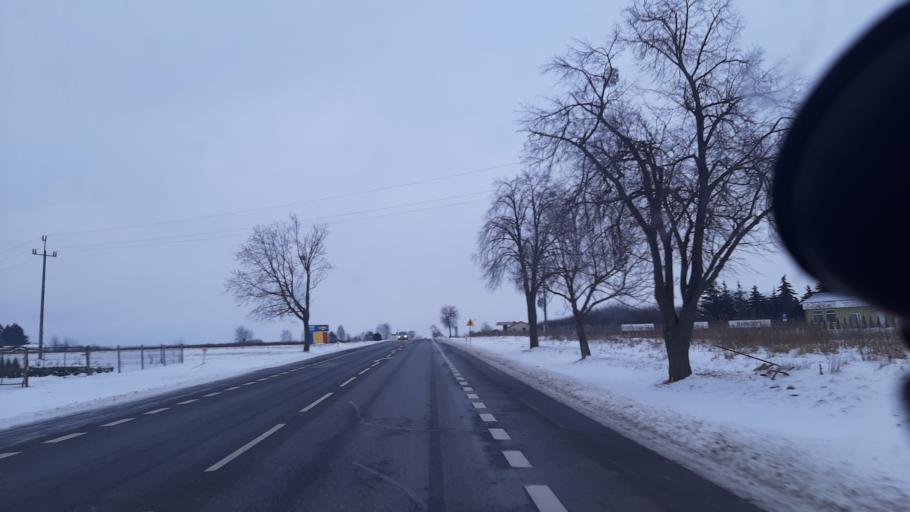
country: PL
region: Lublin Voivodeship
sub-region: Powiat pulawski
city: Markuszow
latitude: 51.3831
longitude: 22.2226
